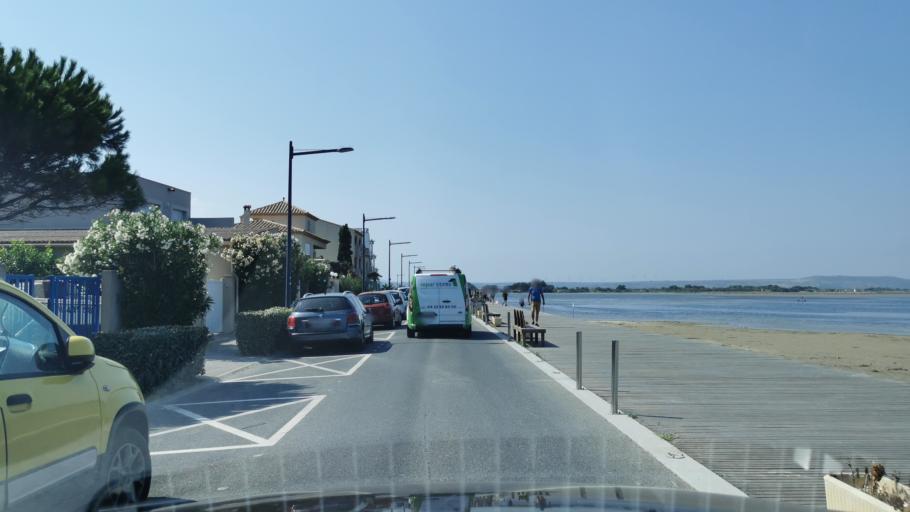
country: FR
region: Languedoc-Roussillon
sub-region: Departement de l'Aude
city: Leucate
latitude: 42.9321
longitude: 3.0372
